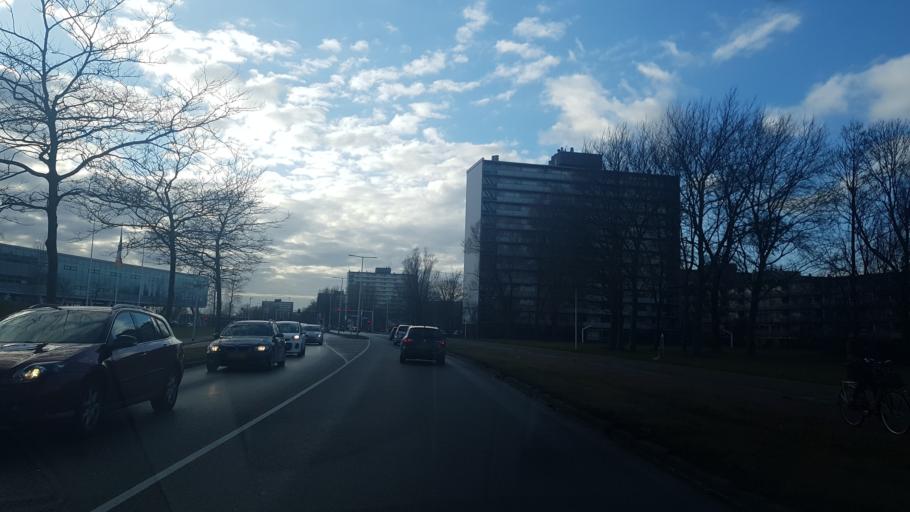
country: NL
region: Friesland
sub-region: Gemeente Leeuwarden
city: Bilgaard
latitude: 53.2130
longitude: 5.8016
